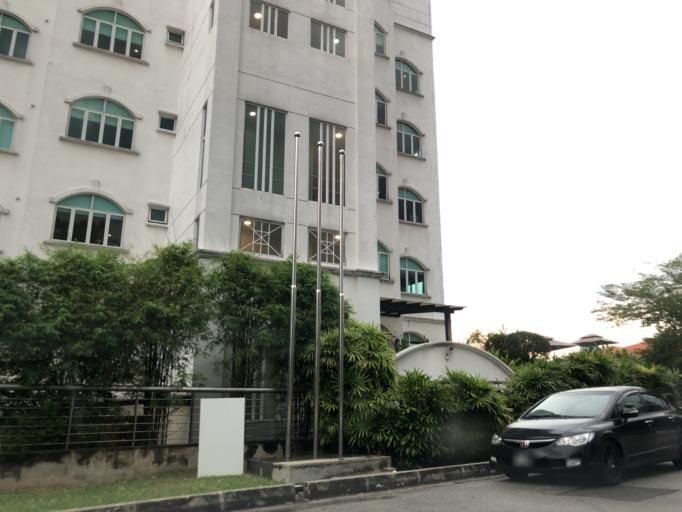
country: SG
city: Singapore
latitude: 1.3035
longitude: 103.8481
